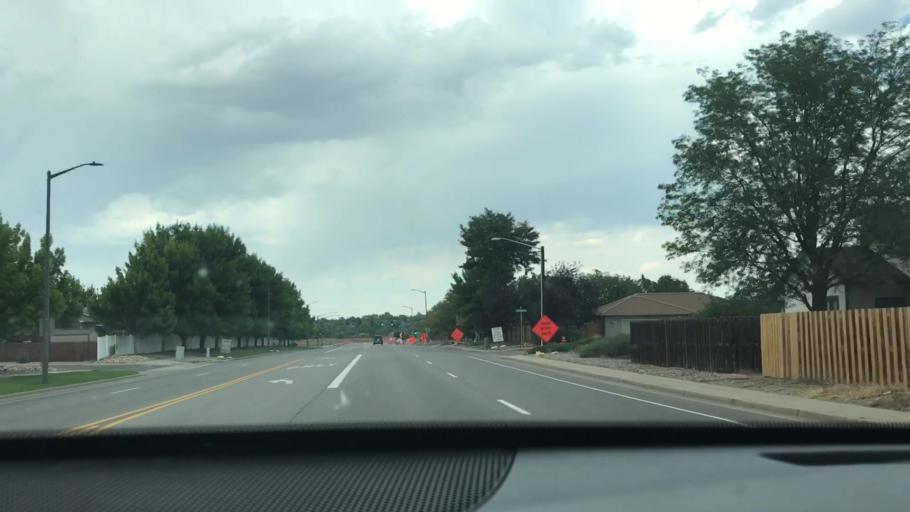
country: US
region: Colorado
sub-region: Larimer County
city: Loveland
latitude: 40.3903
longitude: -105.1160
